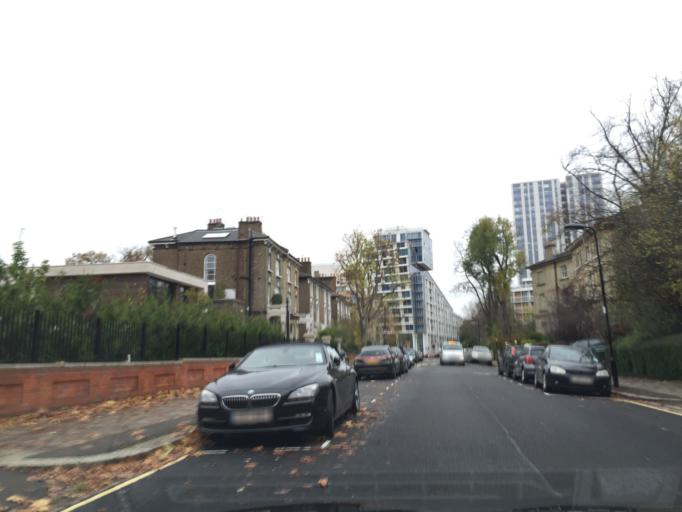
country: GB
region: England
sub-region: Greater London
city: Belsize Park
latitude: 51.5408
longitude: -0.1697
